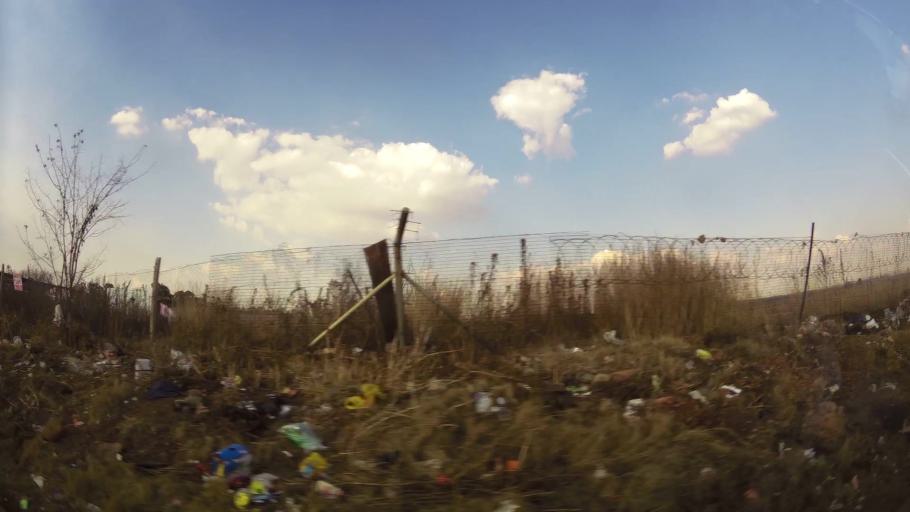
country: ZA
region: Gauteng
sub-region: Ekurhuleni Metropolitan Municipality
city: Germiston
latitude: -26.3704
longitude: 28.2290
